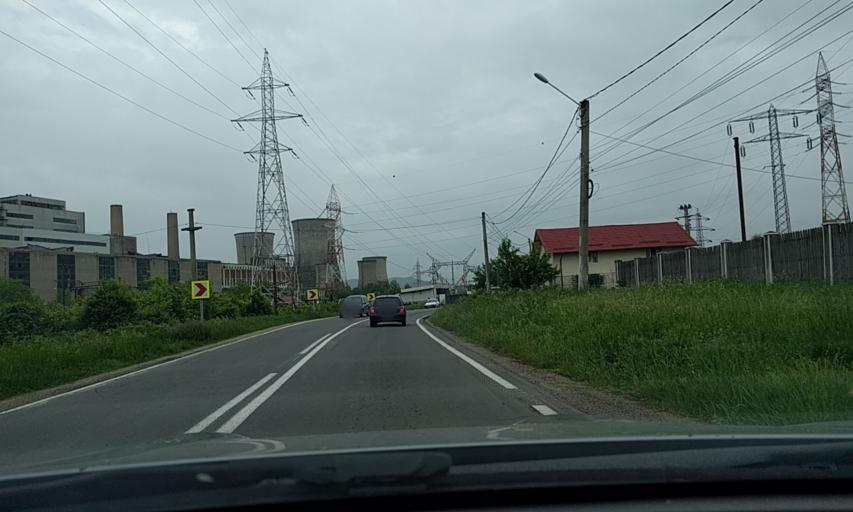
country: RO
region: Dambovita
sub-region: Comuna Doicesti
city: Doicesti
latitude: 44.9989
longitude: 25.4020
